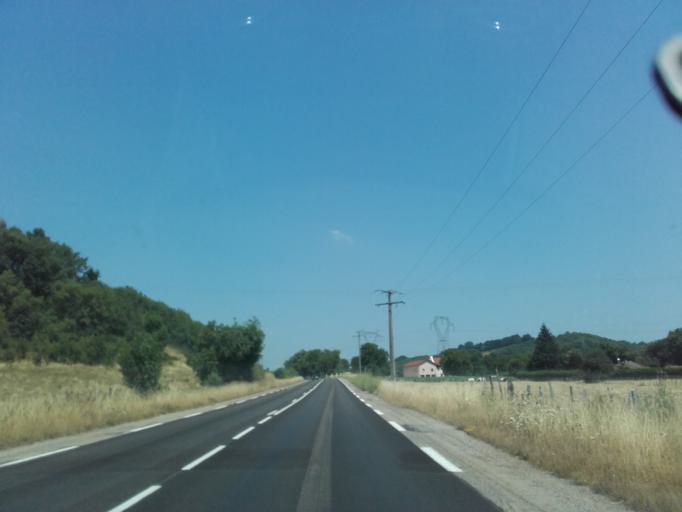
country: FR
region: Rhone-Alpes
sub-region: Departement de l'Isere
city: Champier
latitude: 45.4624
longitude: 5.2929
